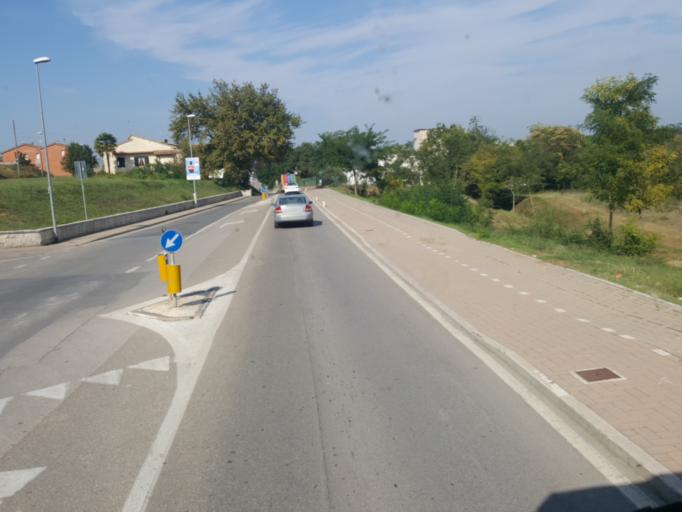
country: IT
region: Tuscany
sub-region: Provincia di Siena
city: Colle di Val d'Elsa
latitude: 43.4047
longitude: 11.1341
